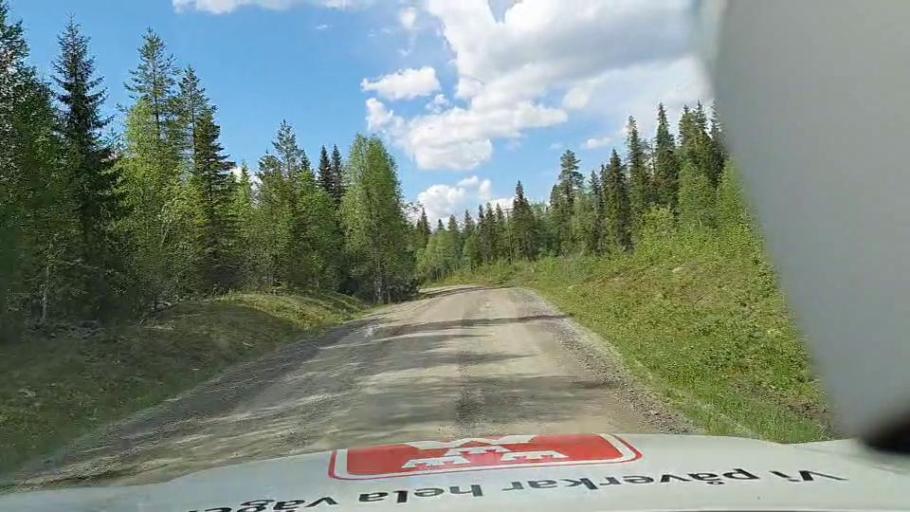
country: SE
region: Vaesterbotten
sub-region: Vilhelmina Kommun
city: Sjoberg
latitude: 64.5415
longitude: 15.7146
